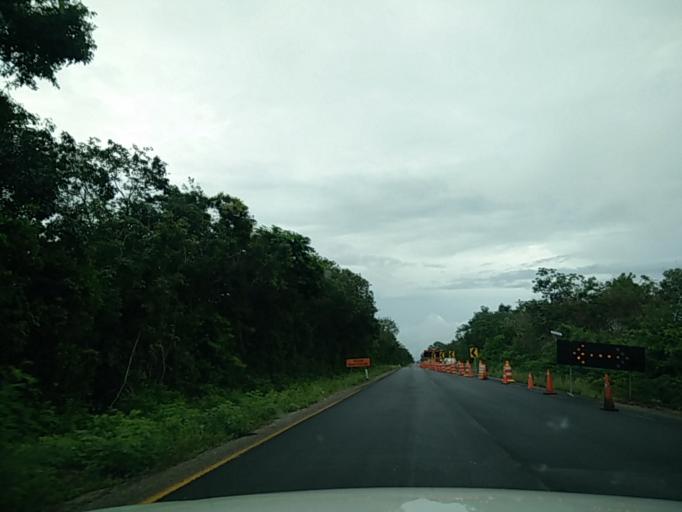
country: MX
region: Quintana Roo
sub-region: Lazaro Cardenas
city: El Tintal
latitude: 20.8971
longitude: -87.4873
